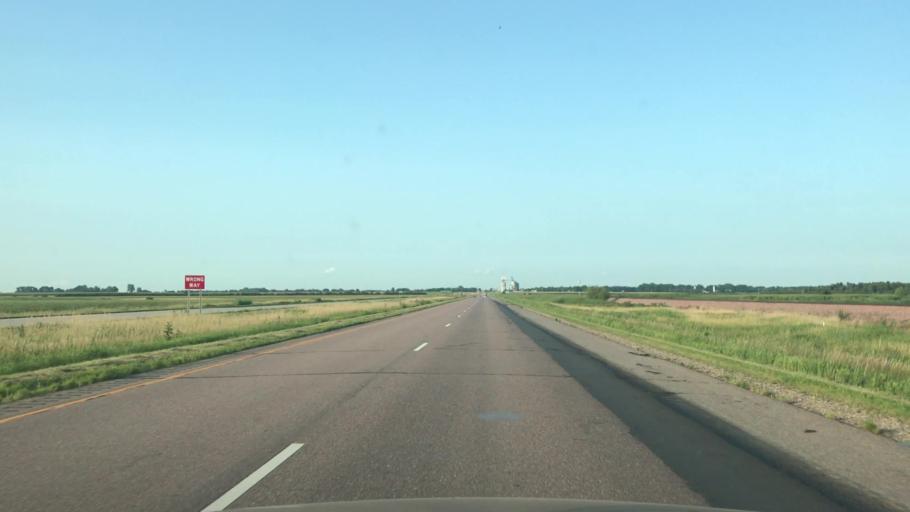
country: US
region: Minnesota
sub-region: Jackson County
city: Lakefield
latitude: 43.7777
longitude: -95.3496
